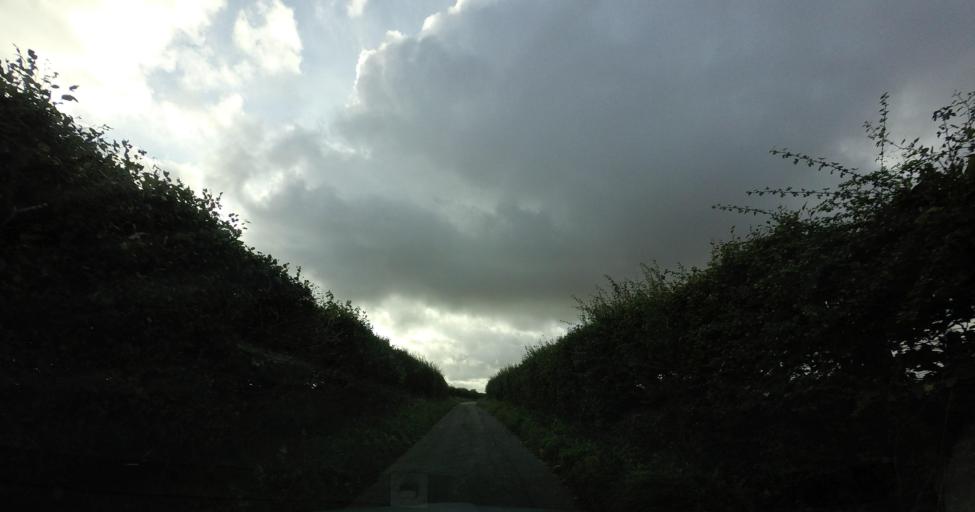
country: GB
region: Scotland
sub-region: Aberdeenshire
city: Whitehills
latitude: 57.6616
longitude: -2.6074
